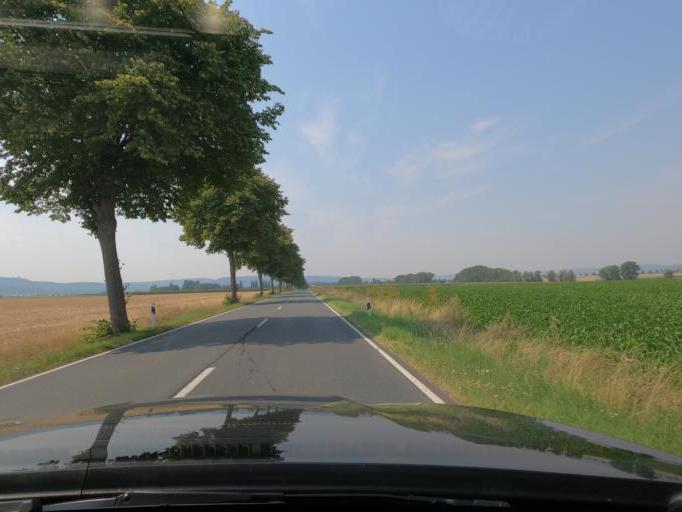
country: DE
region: Lower Saxony
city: Elze
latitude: 52.1702
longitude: 9.6930
